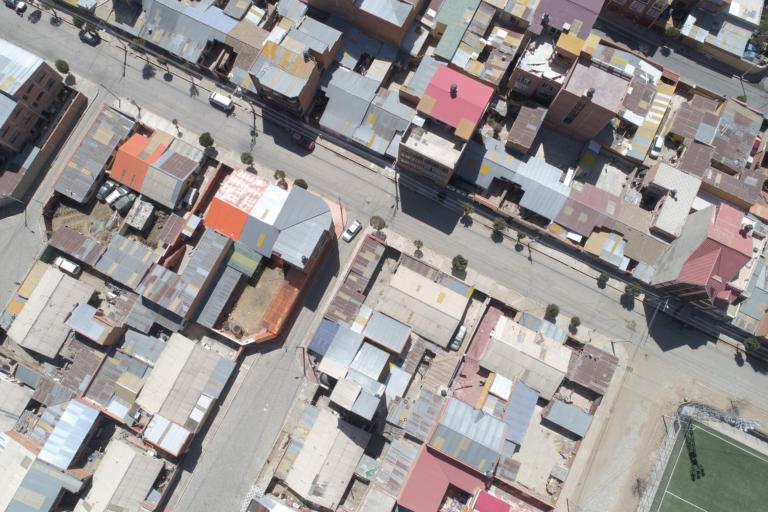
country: BO
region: La Paz
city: La Paz
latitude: -16.5317
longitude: -68.1555
